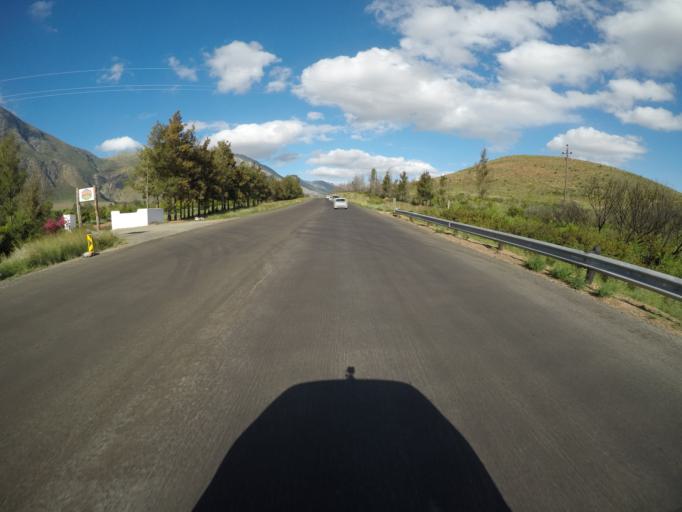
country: ZA
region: Western Cape
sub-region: Cape Winelands District Municipality
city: Ashton
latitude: -33.8706
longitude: 20.1408
